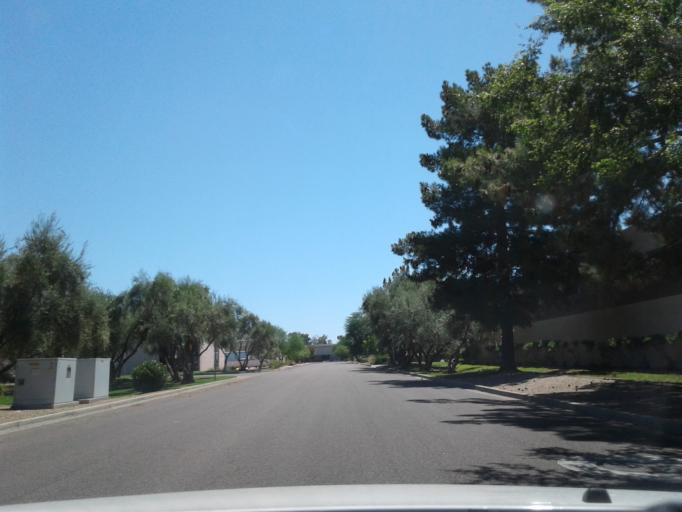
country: US
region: Arizona
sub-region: Maricopa County
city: Guadalupe
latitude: 33.3975
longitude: -112.0180
